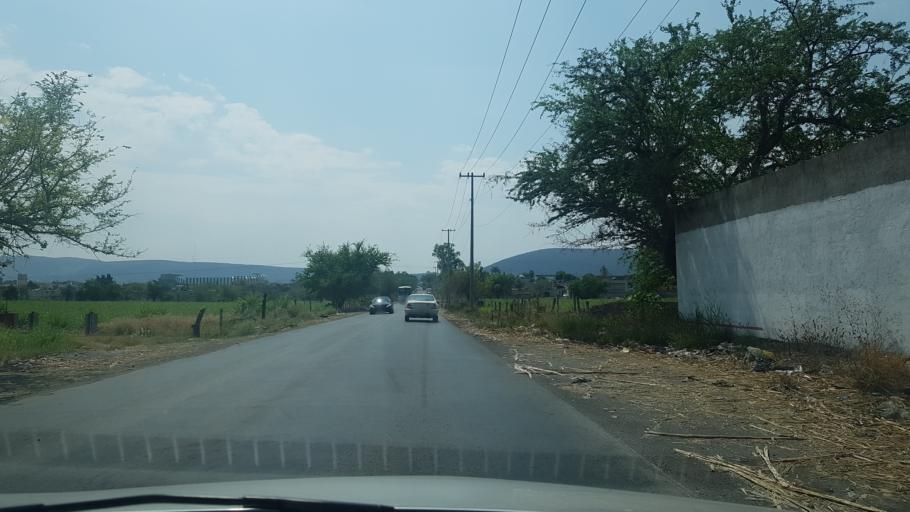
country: MX
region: Morelos
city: Zacatepec
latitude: 18.6588
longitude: -99.1813
